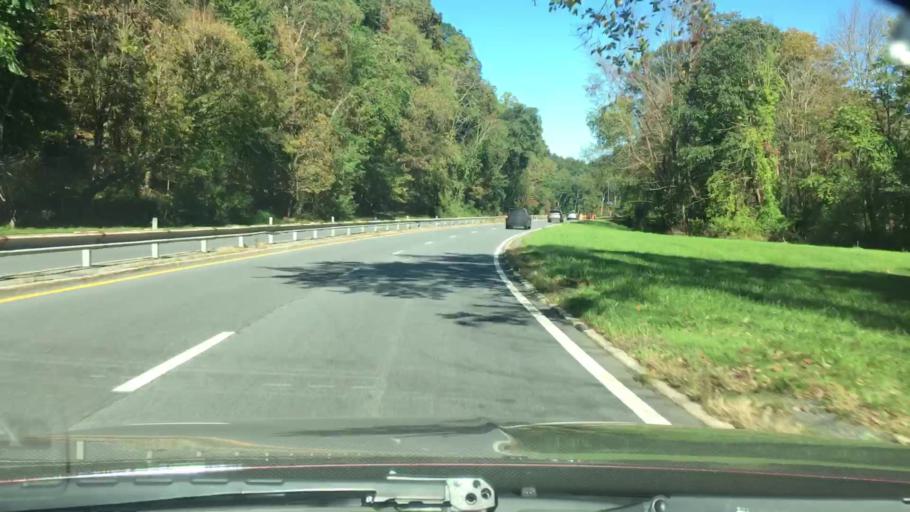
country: US
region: New York
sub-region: Westchester County
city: Mount Kisco
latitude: 41.1984
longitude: -73.7441
